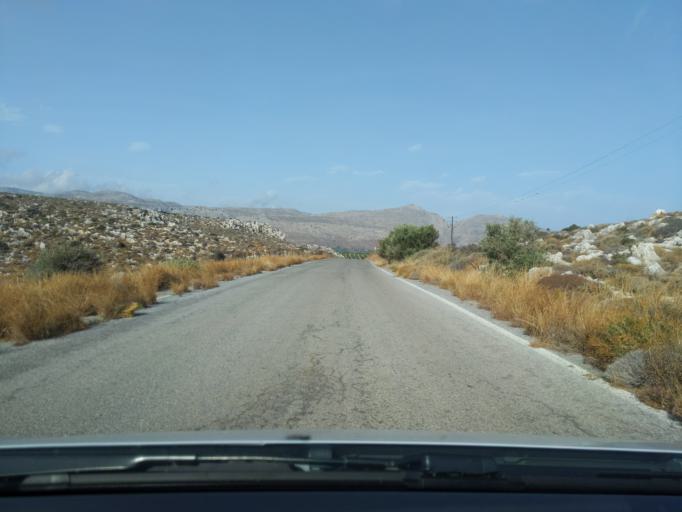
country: GR
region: Crete
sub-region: Nomos Lasithiou
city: Palekastro
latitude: 35.0852
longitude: 26.2530
